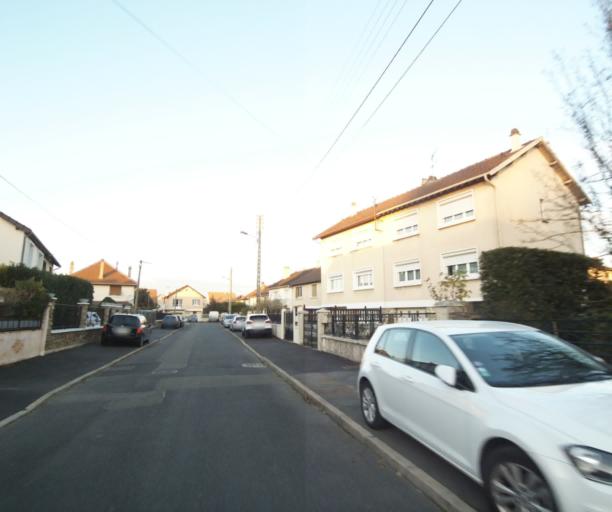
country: FR
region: Ile-de-France
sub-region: Departement du Val-d'Oise
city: Gonesse
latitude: 48.9891
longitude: 2.4445
